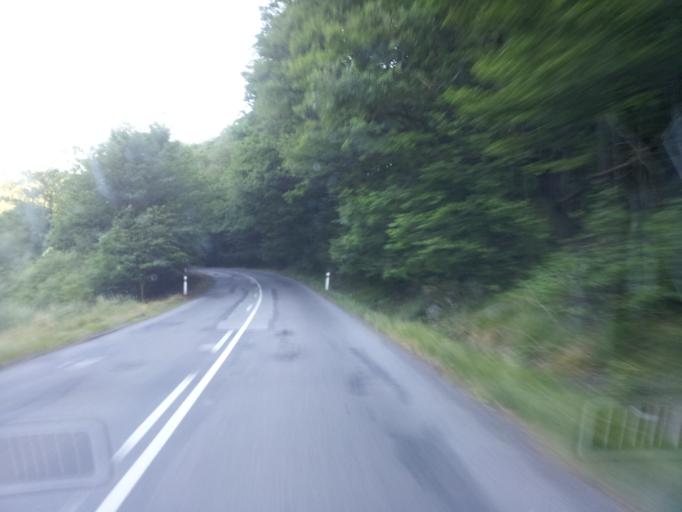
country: SK
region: Banskobystricky
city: Svaety Anton
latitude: 48.3865
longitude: 18.9304
